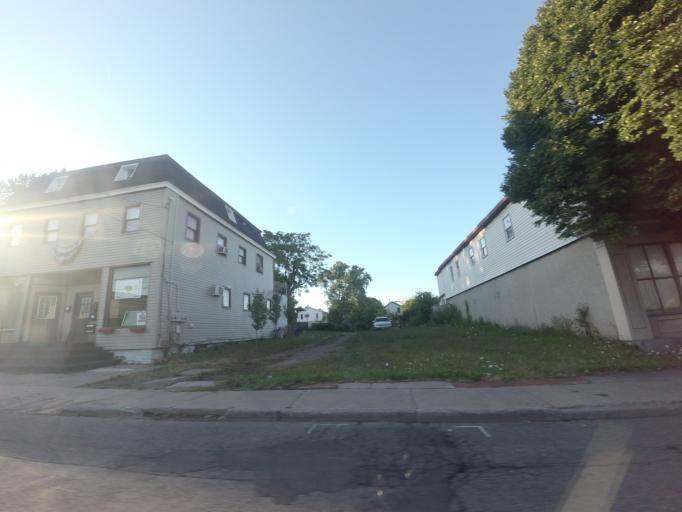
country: US
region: New York
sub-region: Onondaga County
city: East Syracuse
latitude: 43.0641
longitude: -76.0719
